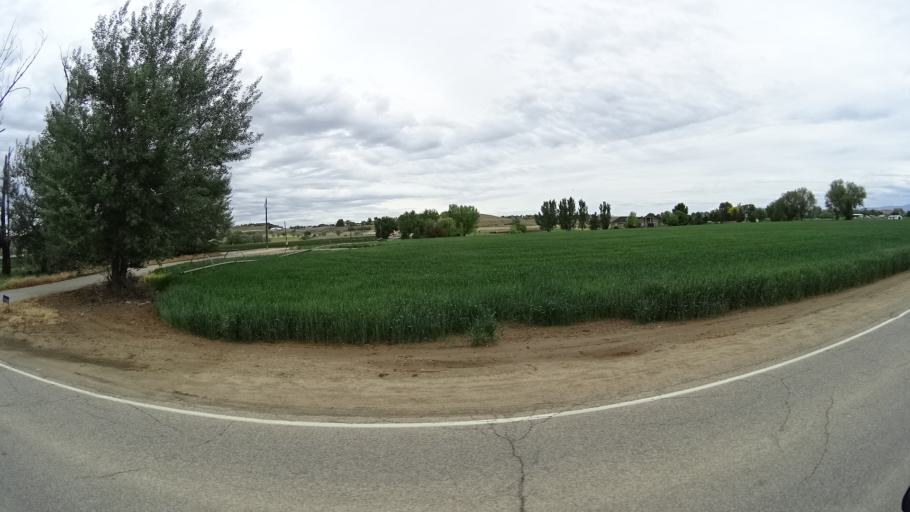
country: US
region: Idaho
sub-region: Ada County
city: Star
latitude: 43.7212
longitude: -116.4778
